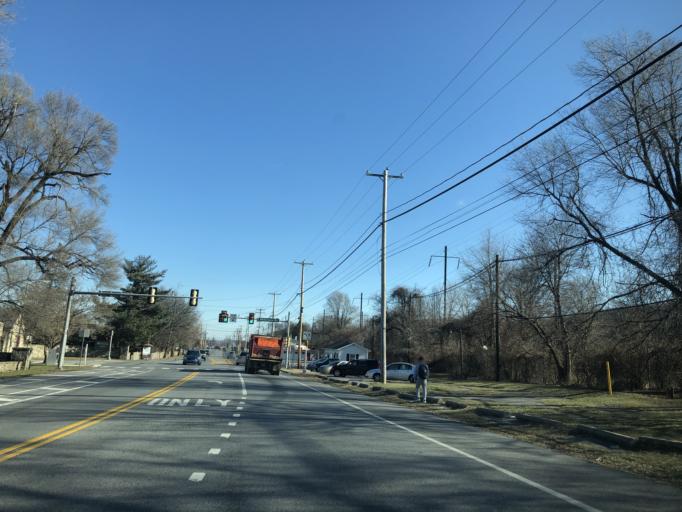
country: US
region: Pennsylvania
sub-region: Chester County
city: Caln
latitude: 39.9882
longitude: -75.7935
